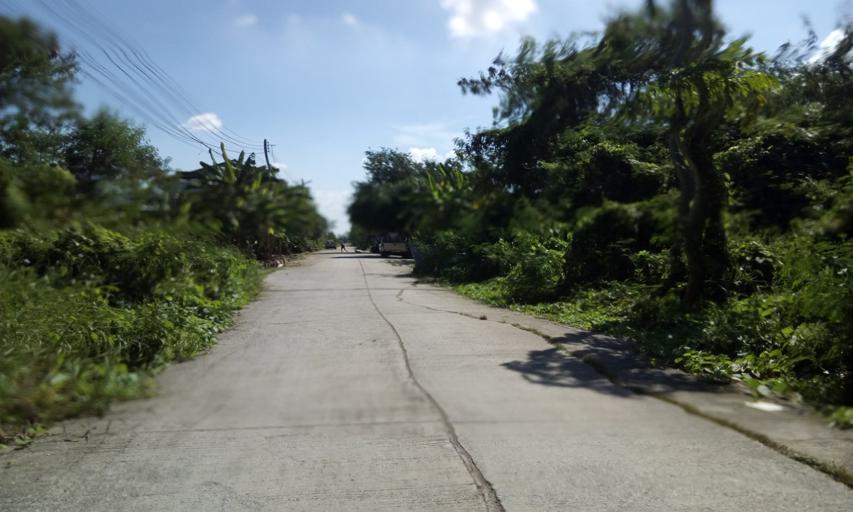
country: TH
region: Pathum Thani
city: Nong Suea
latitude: 14.0660
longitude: 100.8704
